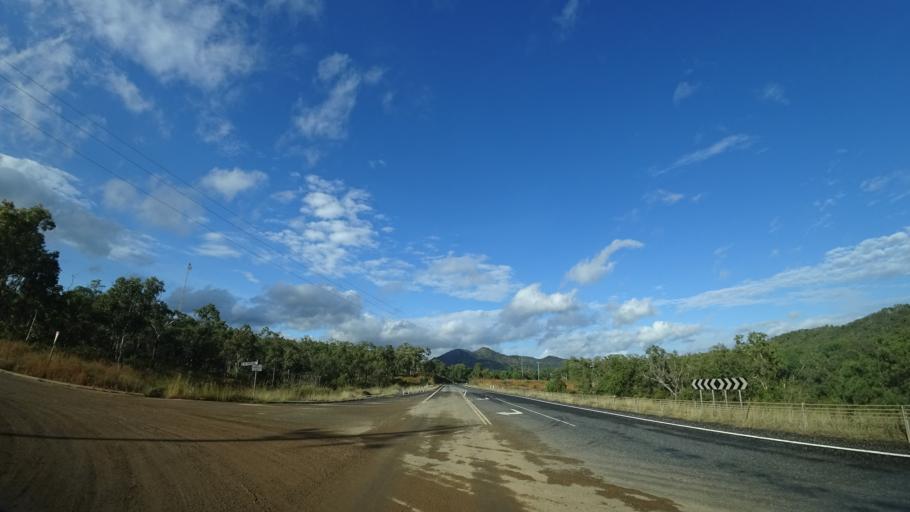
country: AU
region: Queensland
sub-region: Cook
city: Cooktown
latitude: -15.6138
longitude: 145.2211
